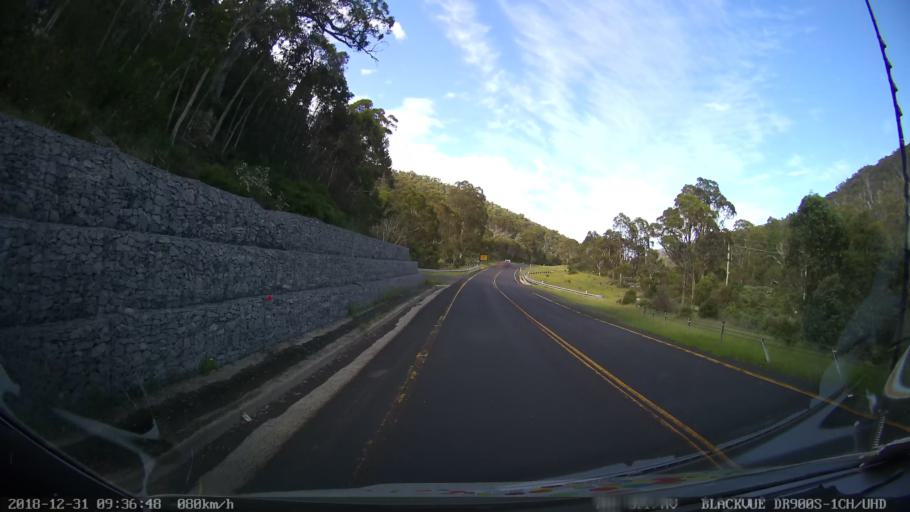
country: AU
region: New South Wales
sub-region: Snowy River
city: Jindabyne
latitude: -36.4615
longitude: 148.3829
